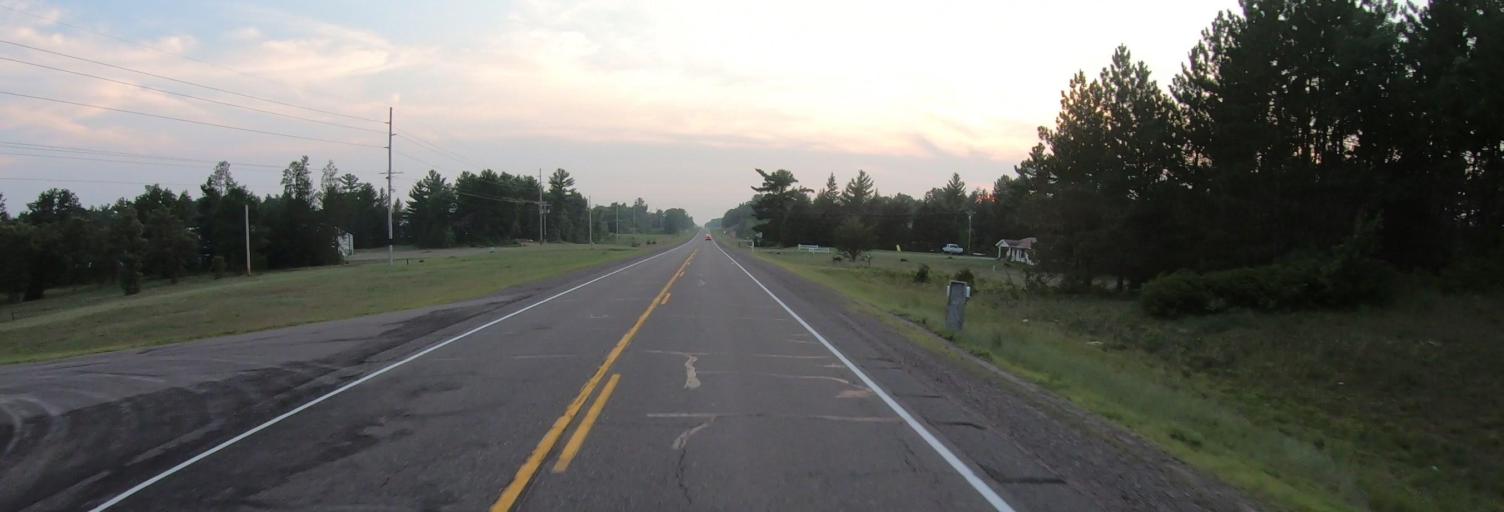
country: US
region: Wisconsin
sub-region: Burnett County
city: Grantsburg
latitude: 45.7731
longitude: -92.7194
